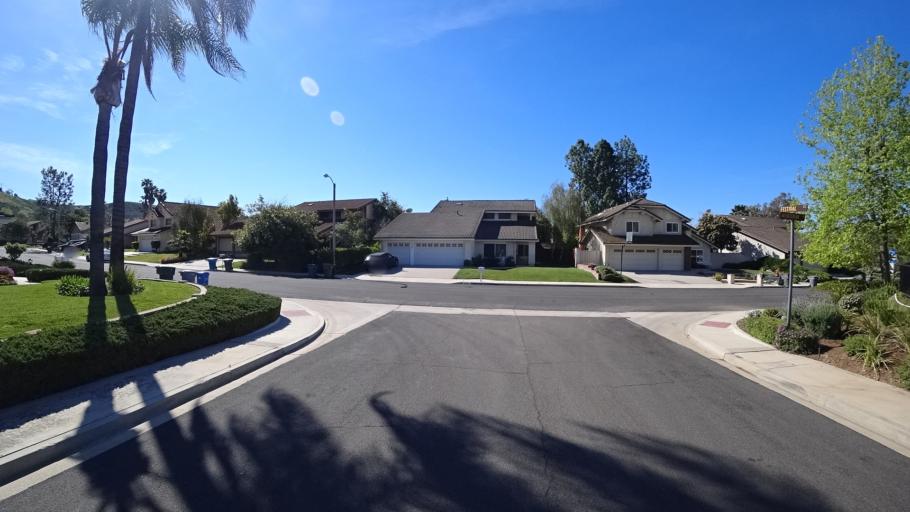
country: US
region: California
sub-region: Ventura County
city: Moorpark
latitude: 34.2292
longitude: -118.8608
